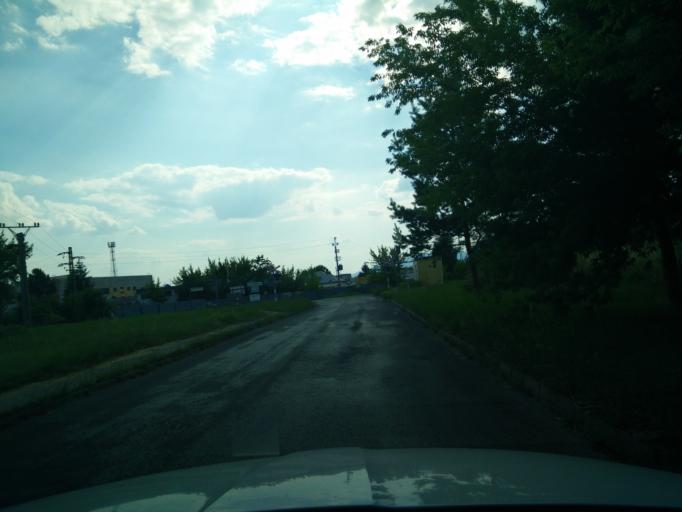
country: SK
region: Nitriansky
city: Prievidza
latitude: 48.7662
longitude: 18.6282
